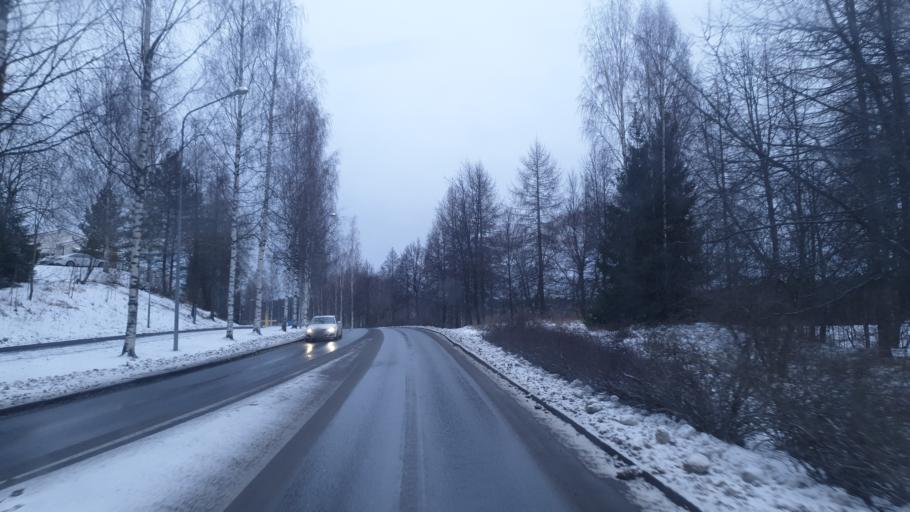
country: FI
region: Northern Savo
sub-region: Kuopio
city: Kuopio
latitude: 62.8350
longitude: 27.6136
